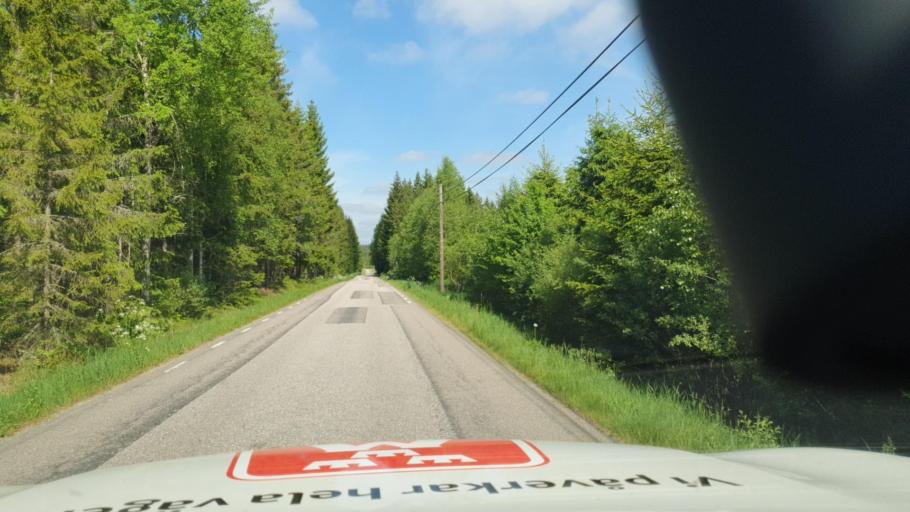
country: SE
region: Vaestra Goetaland
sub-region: Herrljunga Kommun
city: Herrljunga
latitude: 57.9320
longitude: 13.0347
